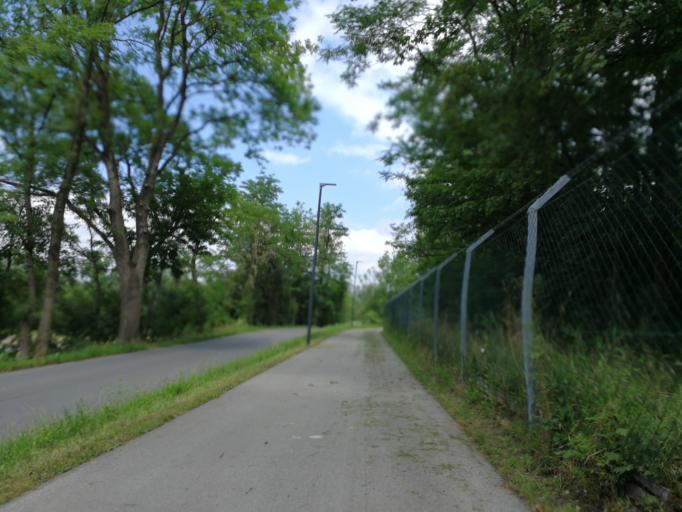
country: DE
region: Bavaria
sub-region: Upper Bavaria
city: Ainring
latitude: 47.7941
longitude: 12.9702
